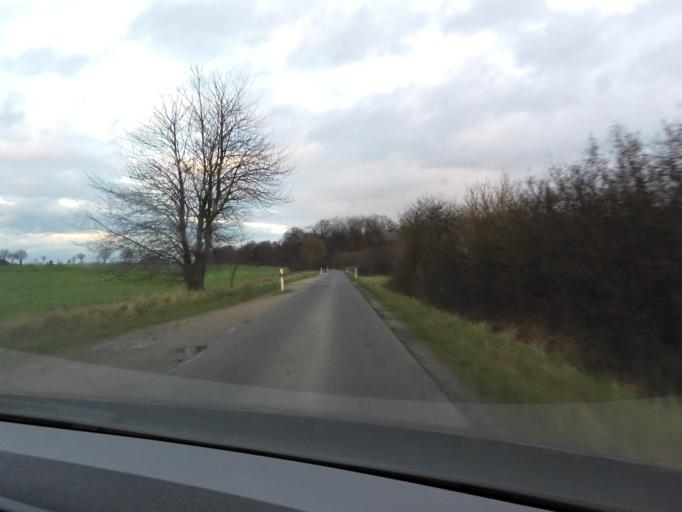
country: DE
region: Schleswig-Holstein
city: Mustin
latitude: 53.6559
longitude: 10.8689
